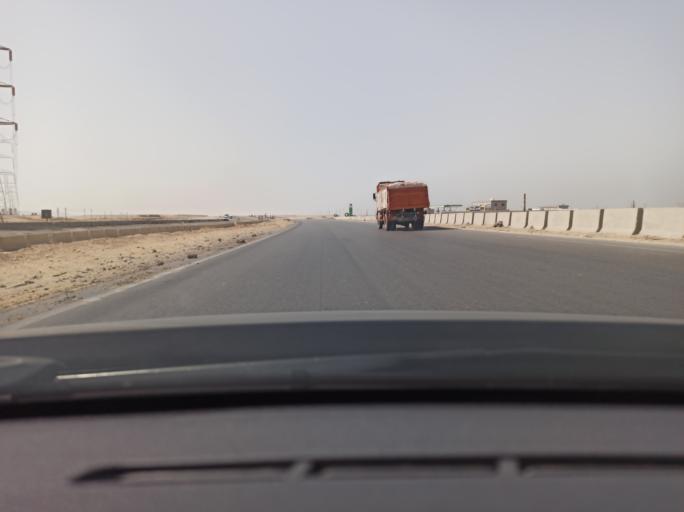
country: EG
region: Muhafazat al Fayyum
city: Al Wasitah
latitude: 29.3844
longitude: 31.3157
